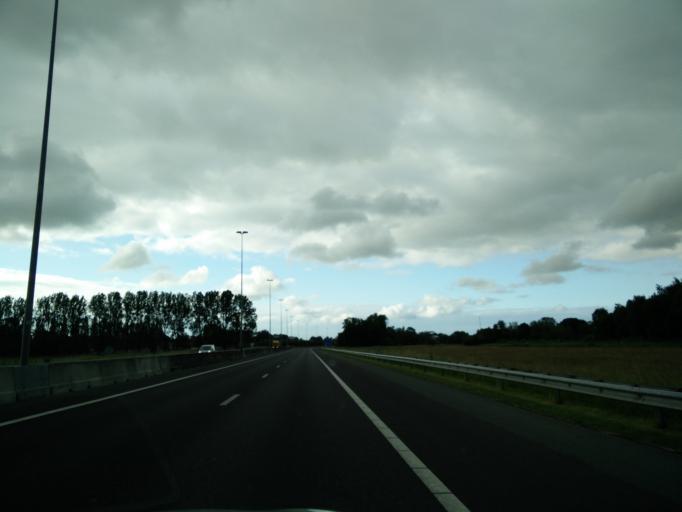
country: NL
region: Groningen
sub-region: Gemeente Haren
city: Haren
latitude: 53.1746
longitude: 6.5861
